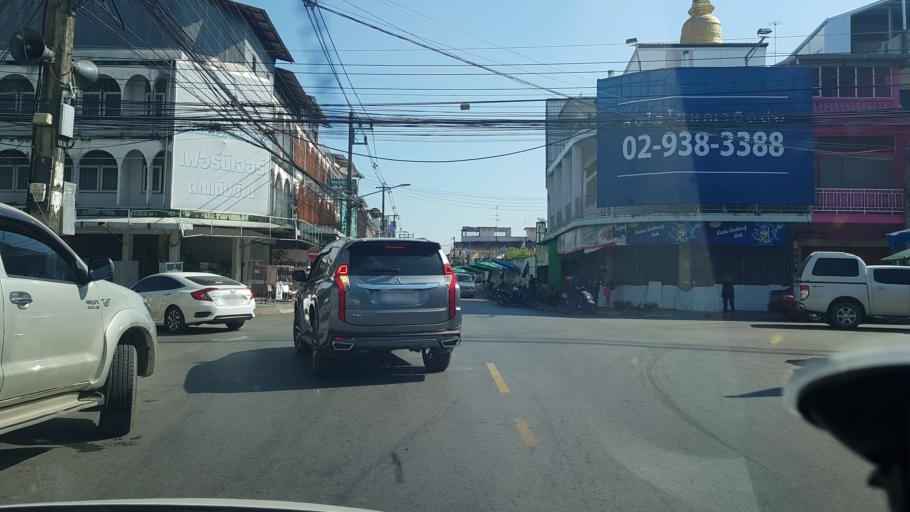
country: TH
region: Chiang Rai
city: Chiang Rai
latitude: 19.9098
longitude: 99.8280
